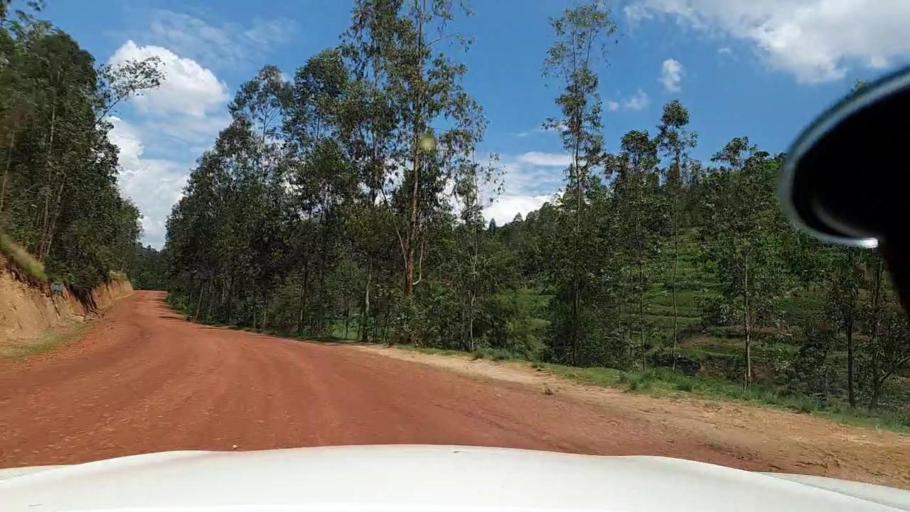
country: RW
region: Northern Province
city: Byumba
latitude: -1.7583
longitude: 29.8694
